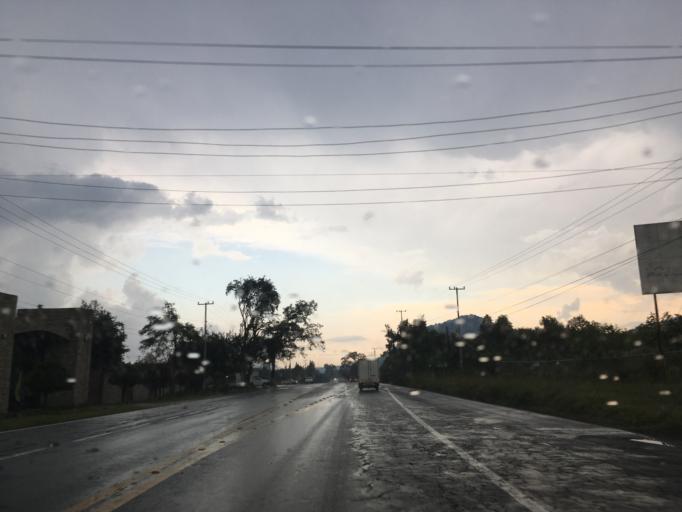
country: MX
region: Michoacan
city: Capacuaro
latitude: 19.4954
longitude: -102.0703
